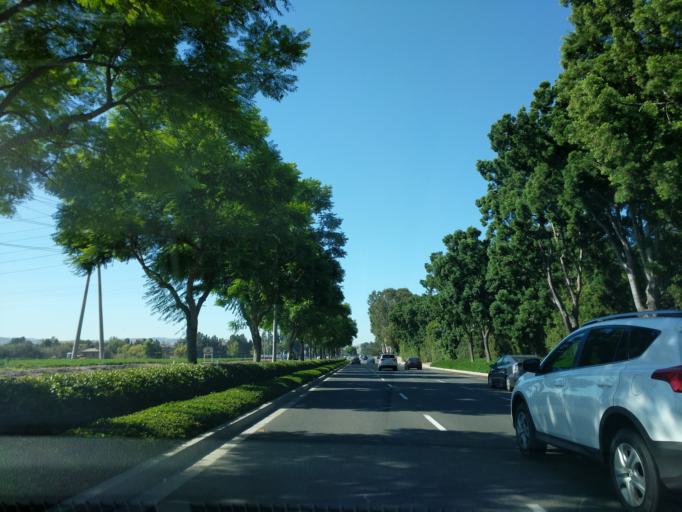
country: US
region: California
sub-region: Orange County
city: Irvine
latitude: 33.6756
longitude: -117.7828
